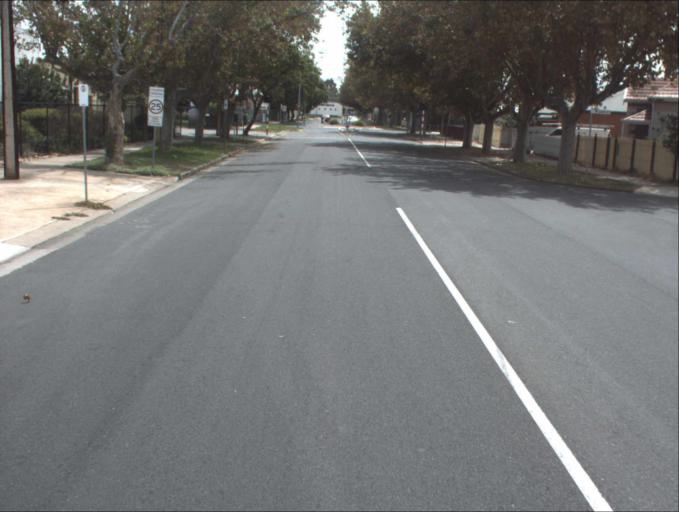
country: AU
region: South Australia
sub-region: Port Adelaide Enfield
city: Alberton
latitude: -34.8566
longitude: 138.5228
